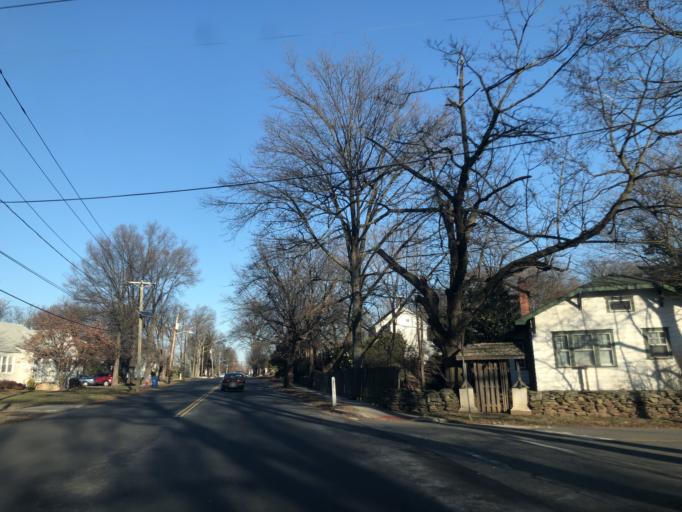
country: US
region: New Jersey
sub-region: Middlesex County
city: Fords
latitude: 40.5371
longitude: -74.3154
